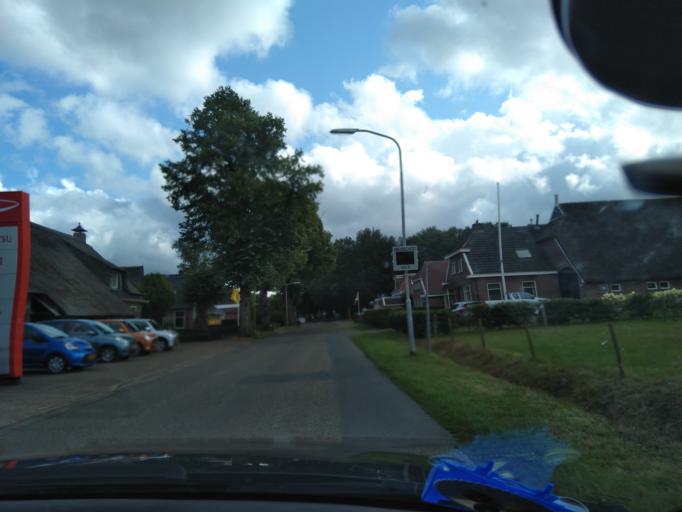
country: NL
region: Drenthe
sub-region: Gemeente Tynaarlo
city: Vries
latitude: 53.0512
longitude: 6.5455
